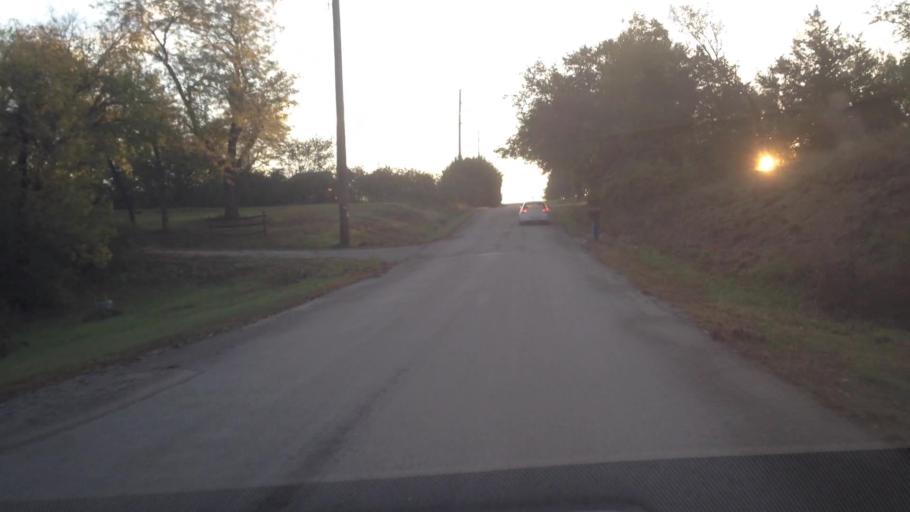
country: US
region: Kansas
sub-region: Johnson County
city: De Soto
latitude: 38.9568
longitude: -95.0173
